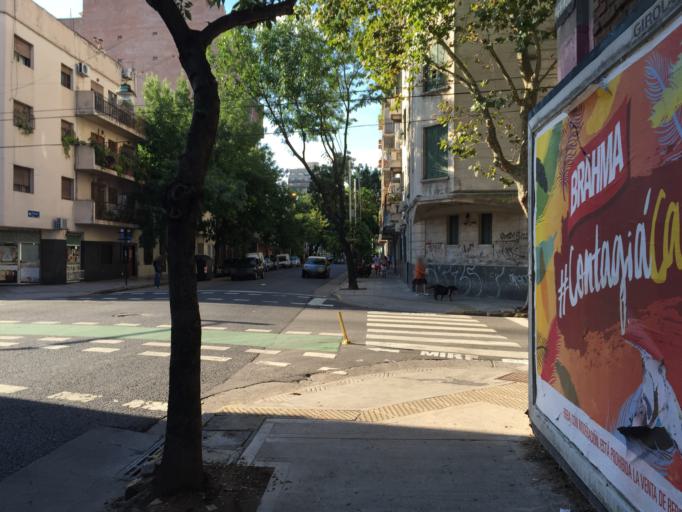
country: AR
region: Buenos Aires F.D.
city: Buenos Aires
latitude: -34.6210
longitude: -58.3985
